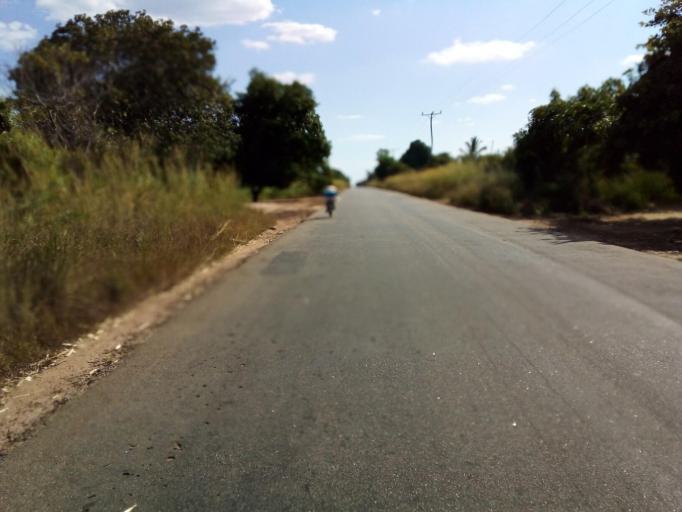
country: MZ
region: Zambezia
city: Quelimane
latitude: -17.5772
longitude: 36.6639
